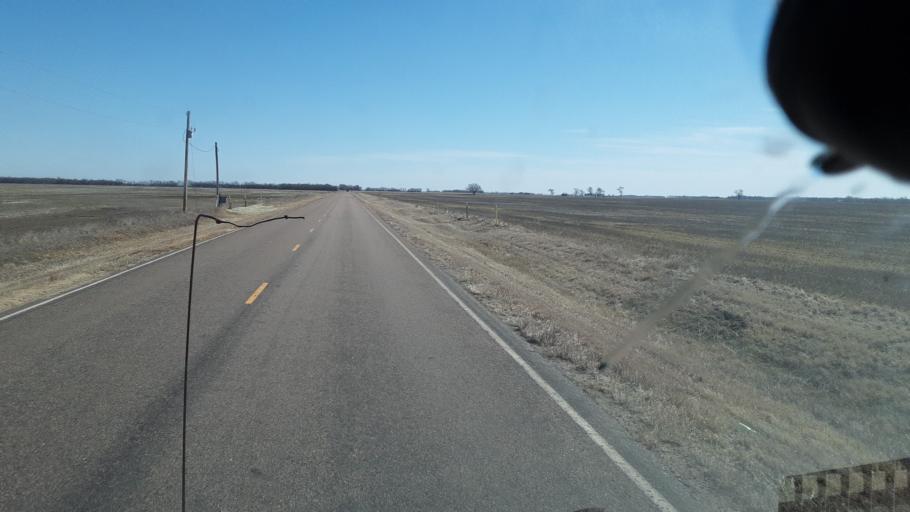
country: US
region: Kansas
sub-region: Rice County
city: Sterling
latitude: 38.2461
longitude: -98.2503
